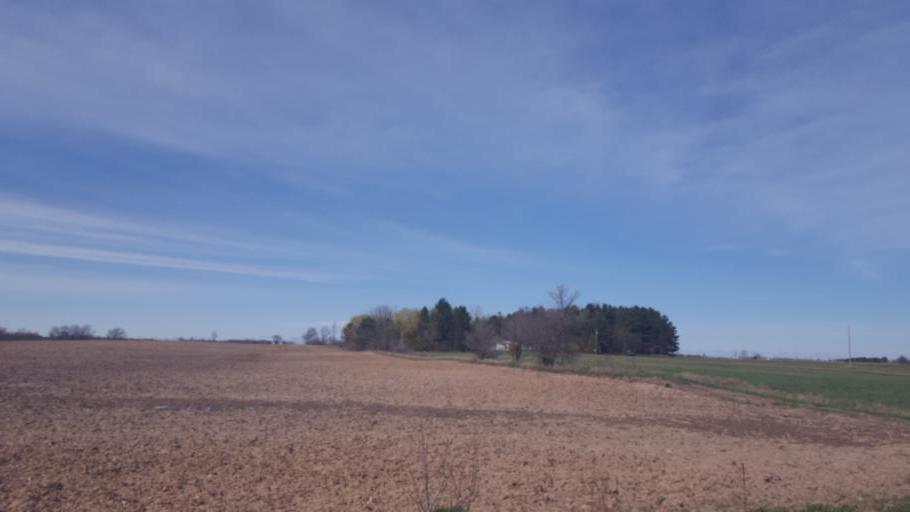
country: US
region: Michigan
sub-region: Gladwin County
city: Gladwin
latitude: 44.0599
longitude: -84.4780
